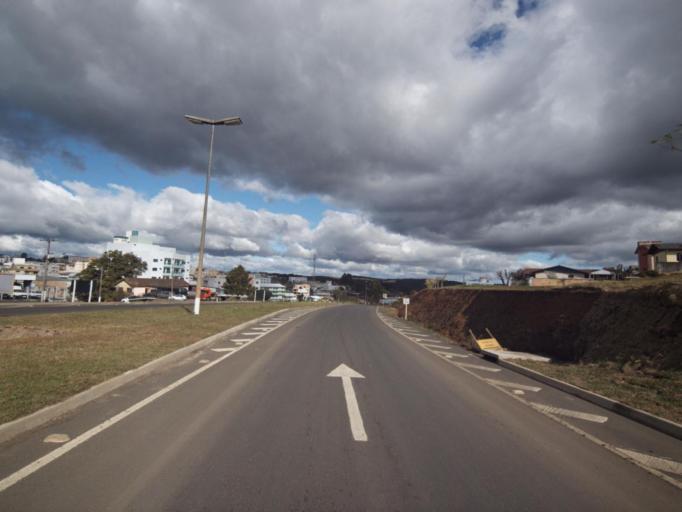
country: BR
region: Santa Catarina
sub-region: Joacaba
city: Joacaba
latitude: -27.0684
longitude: -51.6630
